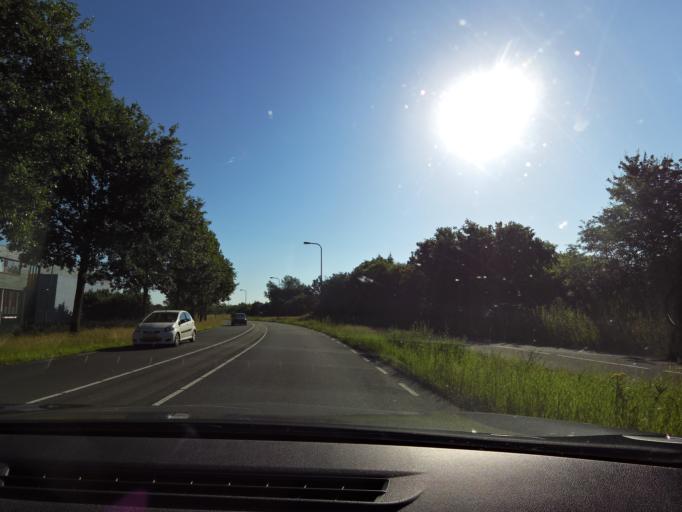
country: NL
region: Overijssel
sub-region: Gemeente Deventer
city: Schalkhaar
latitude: 52.2599
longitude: 6.1939
